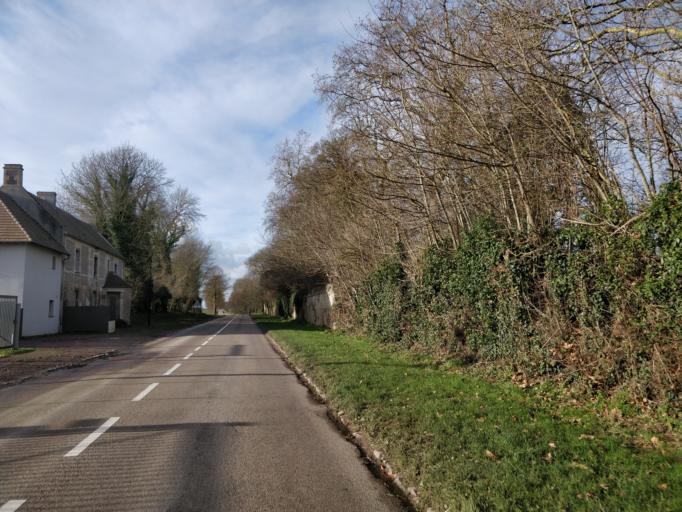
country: FR
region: Lower Normandy
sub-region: Departement du Calvados
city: Rots
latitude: 49.2020
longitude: -0.4840
